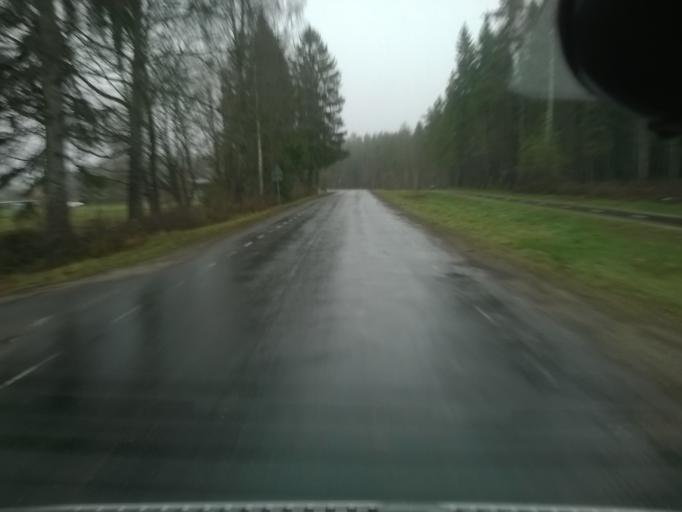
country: EE
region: Raplamaa
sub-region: Kohila vald
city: Kohila
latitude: 59.1721
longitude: 24.6544
